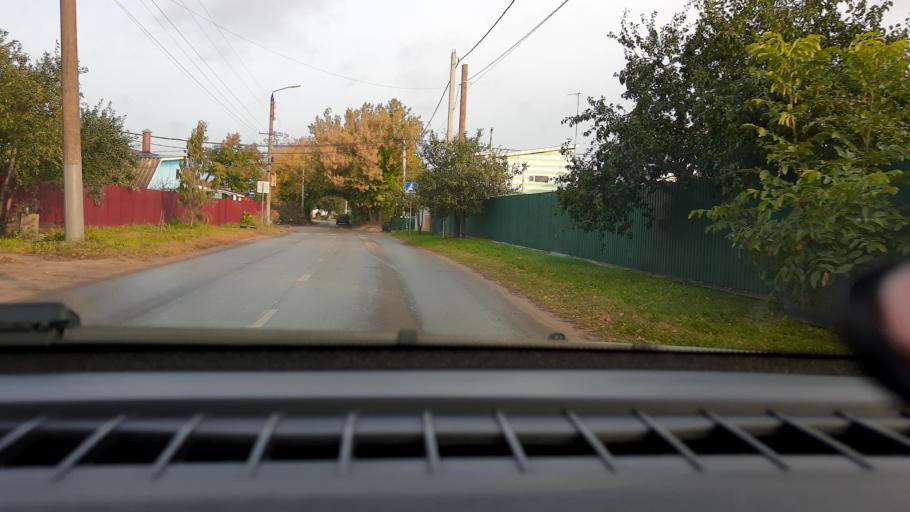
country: RU
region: Nizjnij Novgorod
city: Kstovo
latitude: 56.1893
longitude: 44.1620
